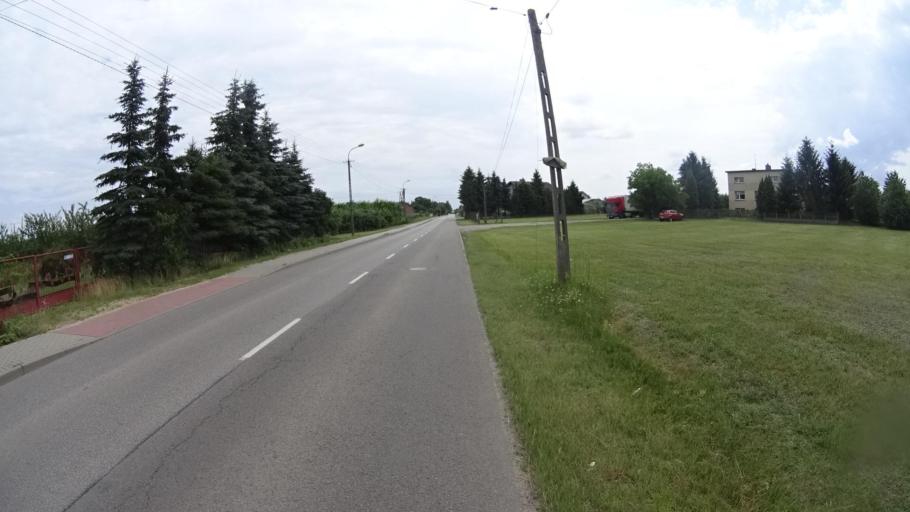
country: PL
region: Masovian Voivodeship
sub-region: Powiat piaseczynski
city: Tarczyn
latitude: 51.9993
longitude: 20.8153
